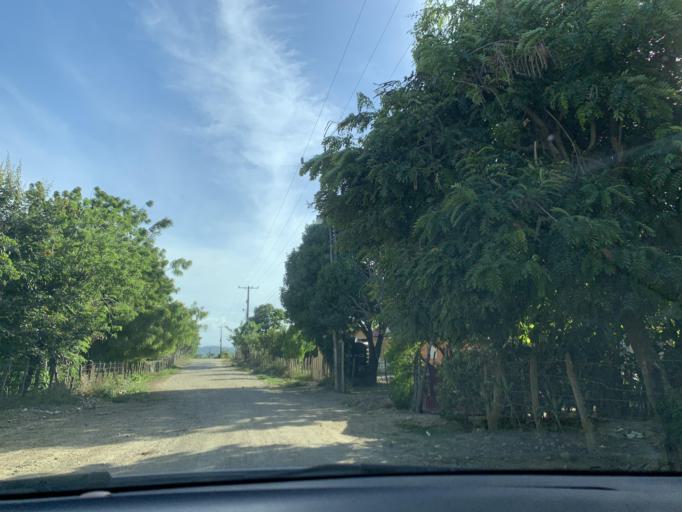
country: DO
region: Puerto Plata
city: Luperon
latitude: 19.8747
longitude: -70.9380
